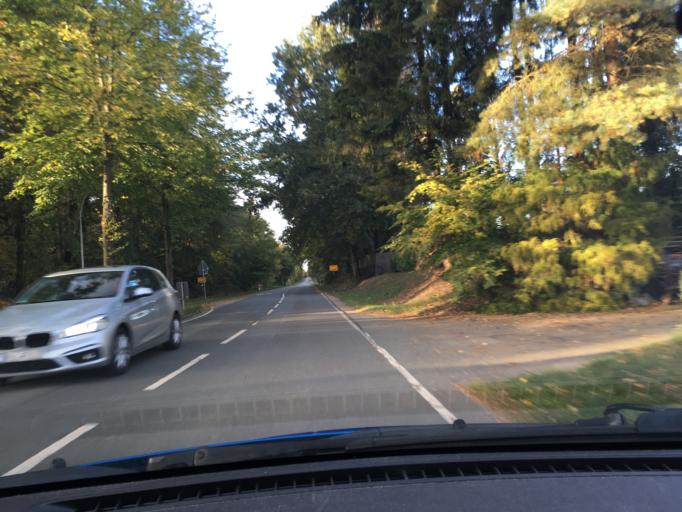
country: DE
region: Lower Saxony
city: Fassberg
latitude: 52.9340
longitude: 10.1344
